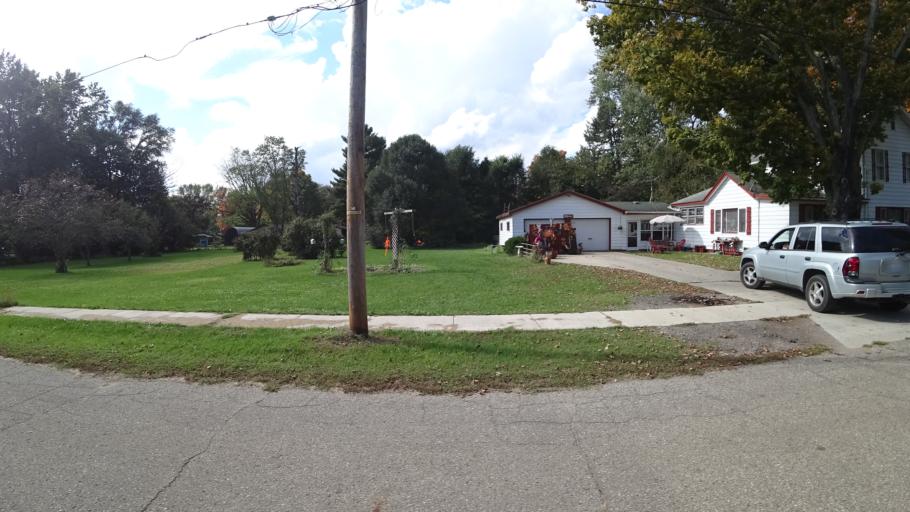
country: US
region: Michigan
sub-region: Saint Joseph County
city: Three Rivers
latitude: 41.9370
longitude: -85.6200
